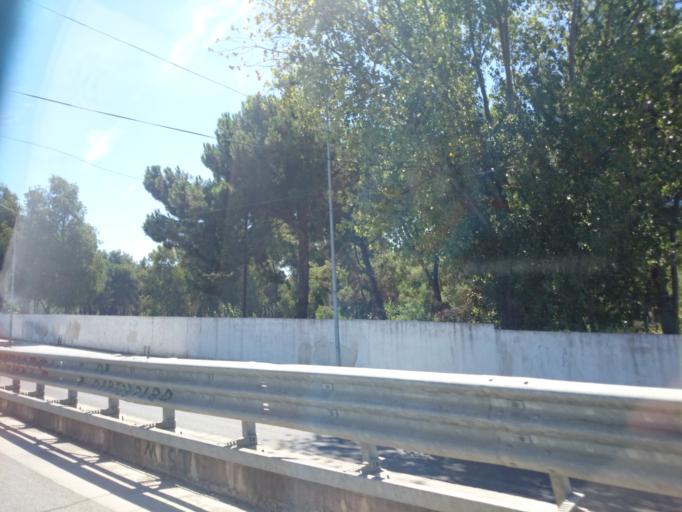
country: AL
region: Durres
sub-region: Rrethi i Durresit
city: Rrashbull
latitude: 41.2904
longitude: 19.5110
